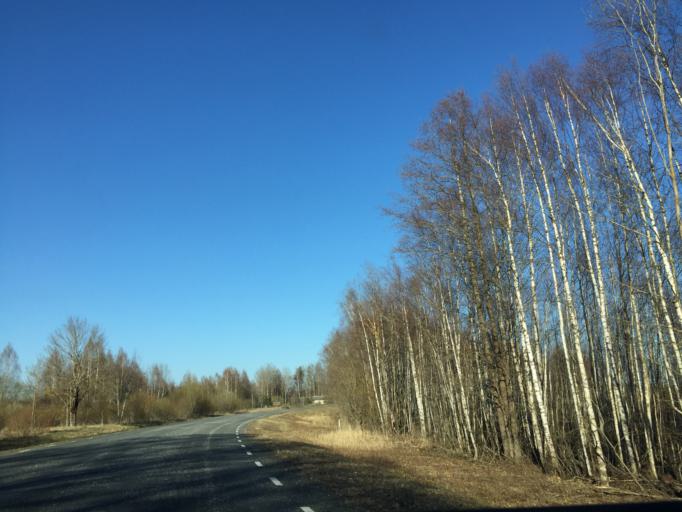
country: RU
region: Pskov
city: Gdov
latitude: 59.0367
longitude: 27.6907
